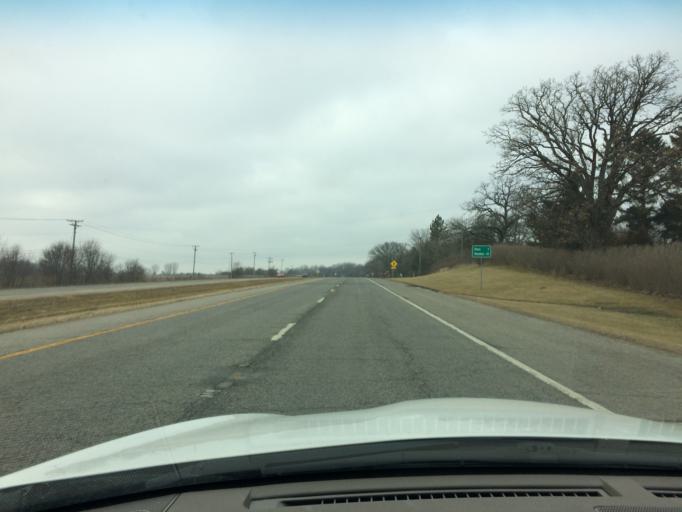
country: US
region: Illinois
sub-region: Kane County
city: Sugar Grove
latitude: 41.7821
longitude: -88.4465
